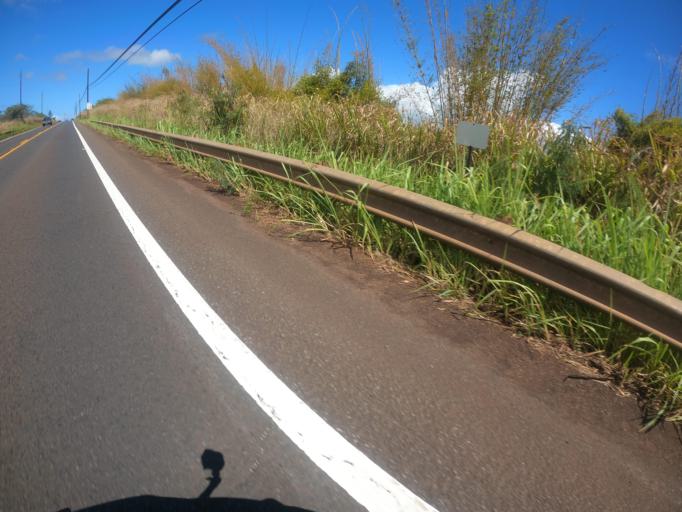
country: US
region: Hawaii
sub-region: Honolulu County
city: Waipi'o Acres
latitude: 21.4482
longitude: -158.0601
